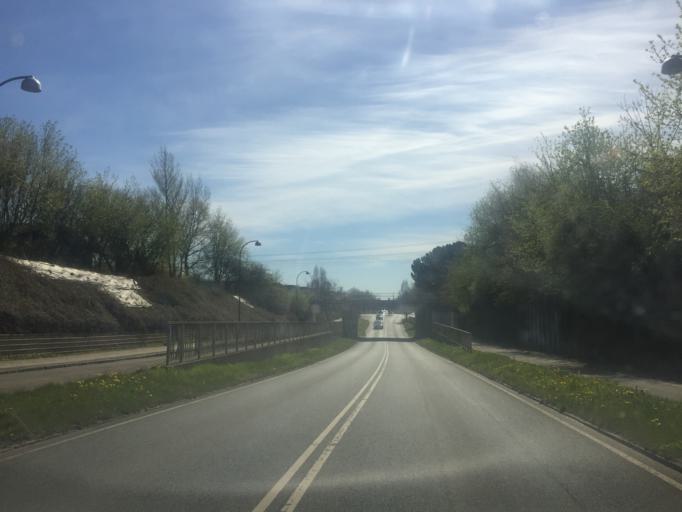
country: DK
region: Capital Region
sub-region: Herlev Kommune
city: Herlev
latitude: 55.7222
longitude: 12.4282
